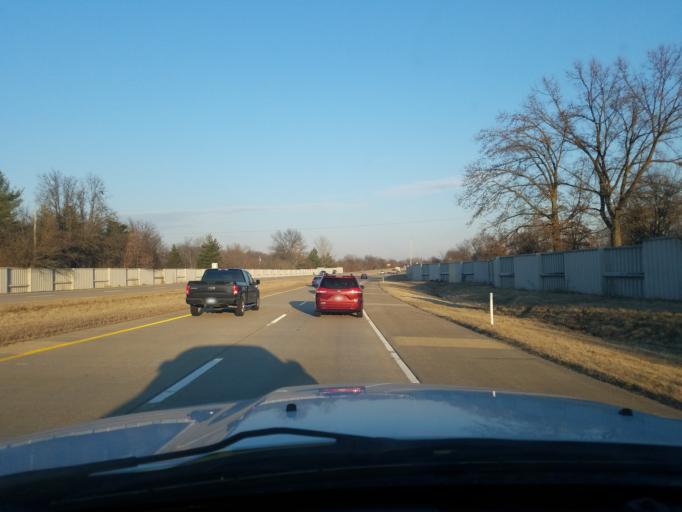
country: US
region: Indiana
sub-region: Warrick County
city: Newburgh
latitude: 37.9492
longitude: -87.4665
